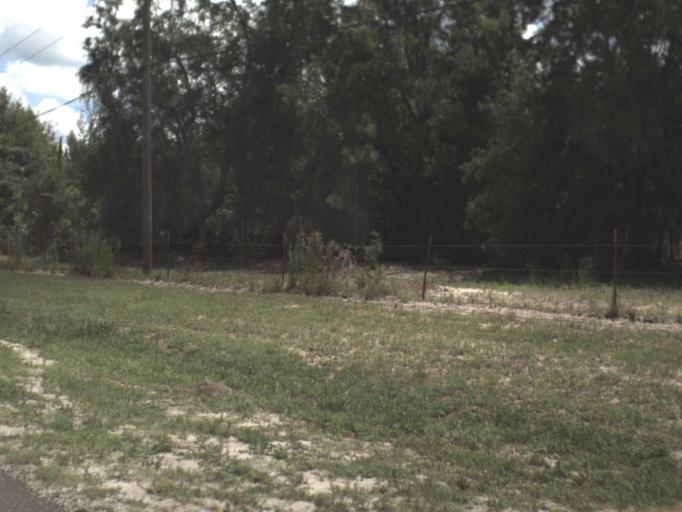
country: US
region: Florida
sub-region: Clay County
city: Keystone Heights
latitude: 29.7195
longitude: -82.0453
